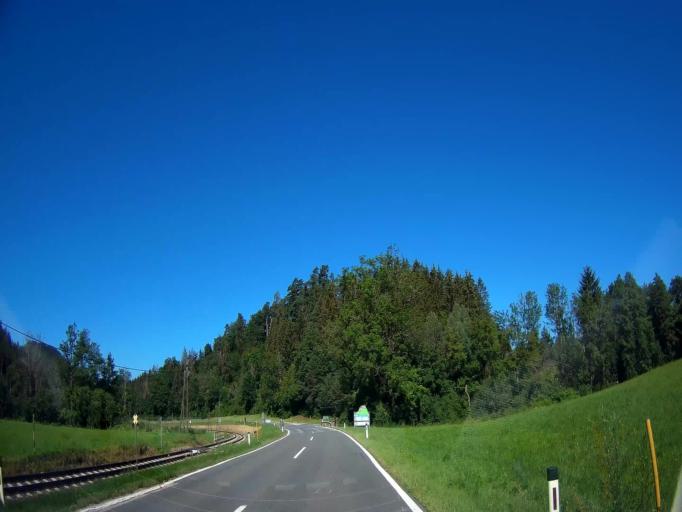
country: AT
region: Carinthia
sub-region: Politischer Bezirk Sankt Veit an der Glan
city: Bruckl
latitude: 46.7621
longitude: 14.4904
